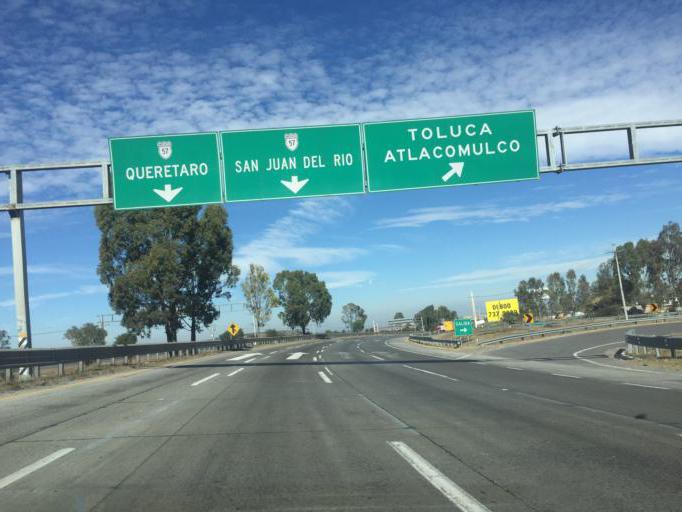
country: MX
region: Queretaro
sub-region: San Juan del Rio
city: Paso de Mata
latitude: 20.2987
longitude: -99.9330
